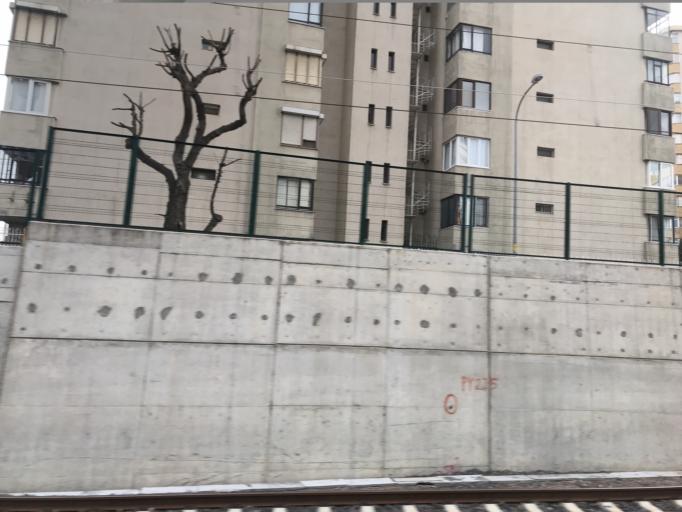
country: TR
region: Istanbul
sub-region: Atasehir
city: Atasehir
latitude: 40.9599
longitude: 29.0878
